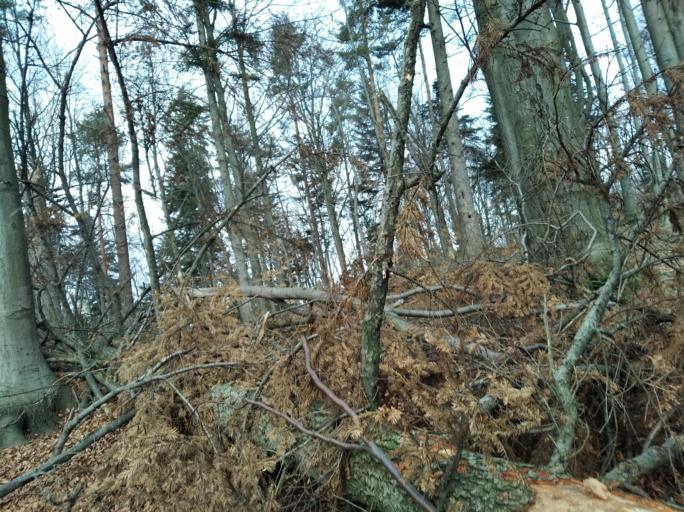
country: PL
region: Subcarpathian Voivodeship
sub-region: Powiat krosnienski
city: Korczyna
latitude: 49.7764
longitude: 21.8080
